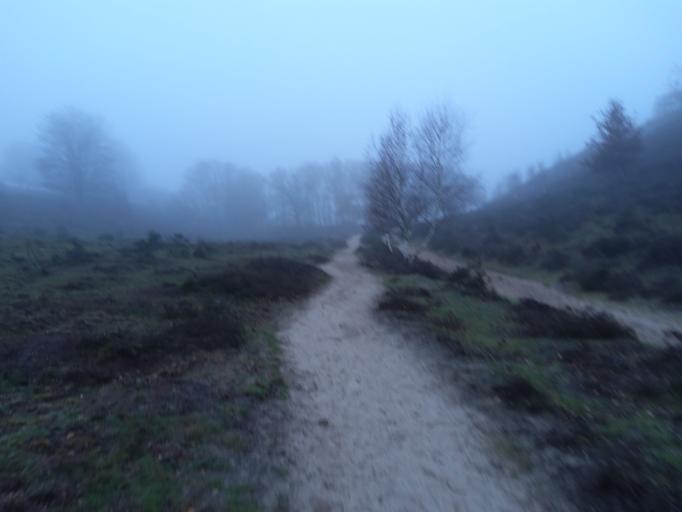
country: NL
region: Gelderland
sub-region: Gemeente Rheden
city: Rheden
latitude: 52.0241
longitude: 6.0172
